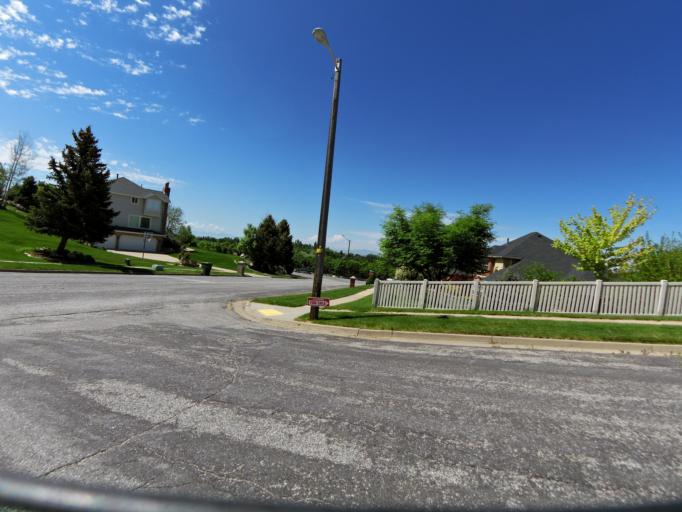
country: US
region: Utah
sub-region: Weber County
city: Washington Terrace
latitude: 41.1718
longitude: -111.9430
